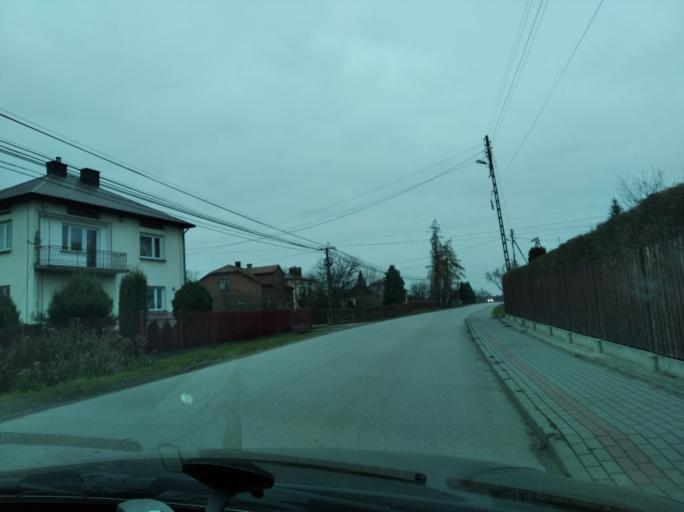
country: PL
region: Subcarpathian Voivodeship
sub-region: Powiat lancucki
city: Rakszawa
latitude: 50.1585
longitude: 22.2397
